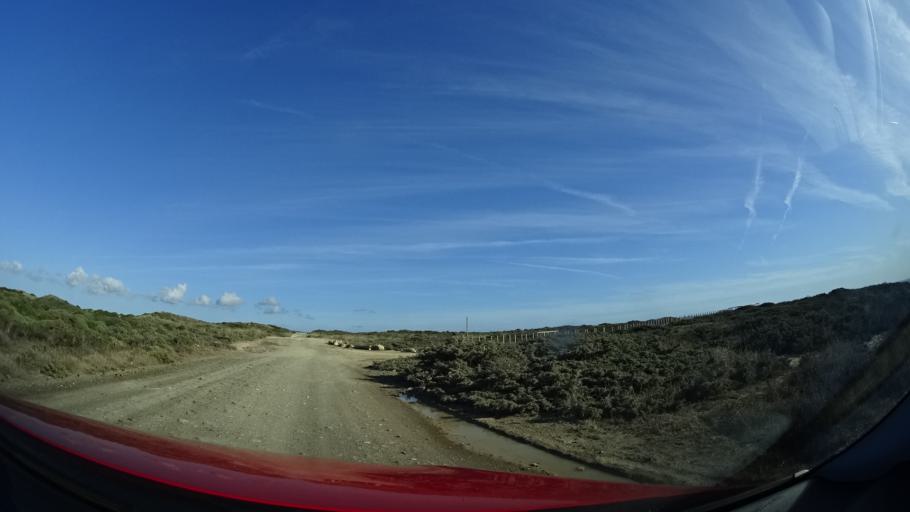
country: PT
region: Faro
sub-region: Vila do Bispo
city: Vila do Bispo
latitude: 37.1942
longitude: -8.9139
